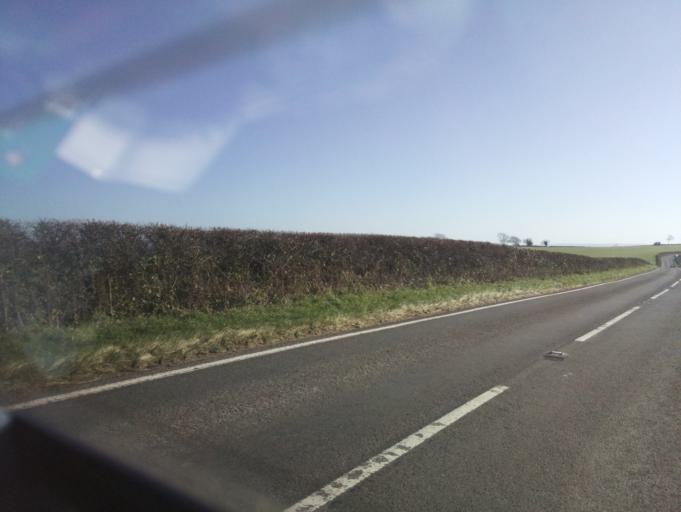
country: GB
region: England
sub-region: Dorset
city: Dorchester
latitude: 50.8219
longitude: -2.4600
